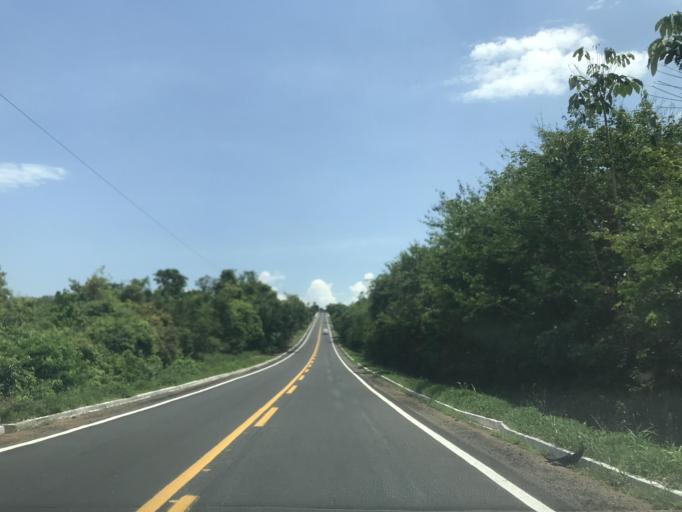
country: BR
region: Goias
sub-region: Bela Vista De Goias
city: Bela Vista de Goias
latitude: -17.1227
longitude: -48.6679
